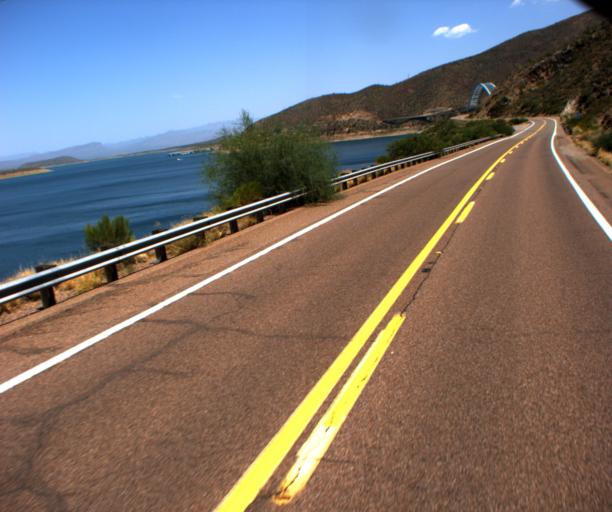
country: US
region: Arizona
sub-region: Gila County
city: Tonto Basin
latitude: 33.6809
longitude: -111.1659
